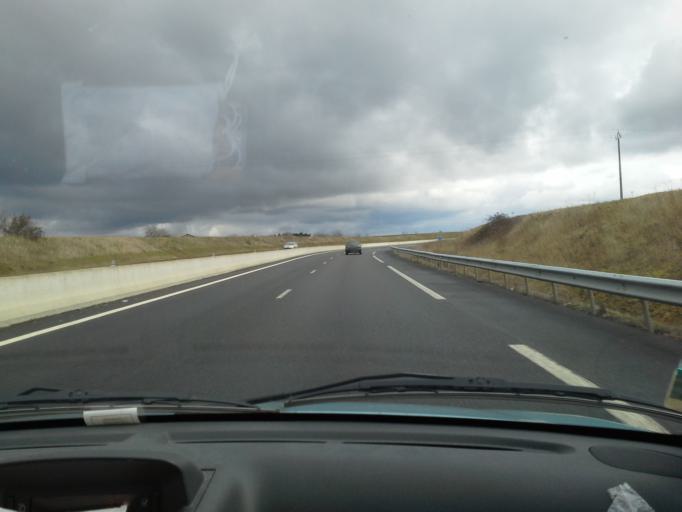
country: FR
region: Centre
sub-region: Departement du Loir-et-Cher
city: Saint-Sulpice-de-Pommeray
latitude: 47.6670
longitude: 1.2386
